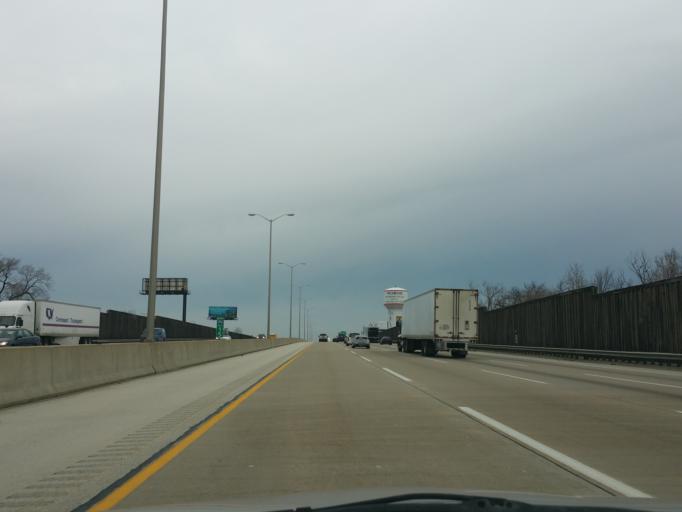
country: US
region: Illinois
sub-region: Cook County
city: Chicago Ridge
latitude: 41.6878
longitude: -87.7817
